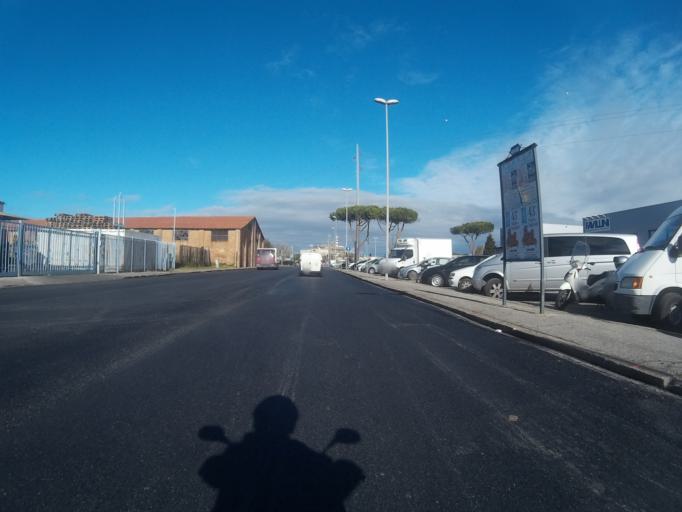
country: IT
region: Tuscany
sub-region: Provincia di Livorno
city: Livorno
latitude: 43.5632
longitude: 10.3420
